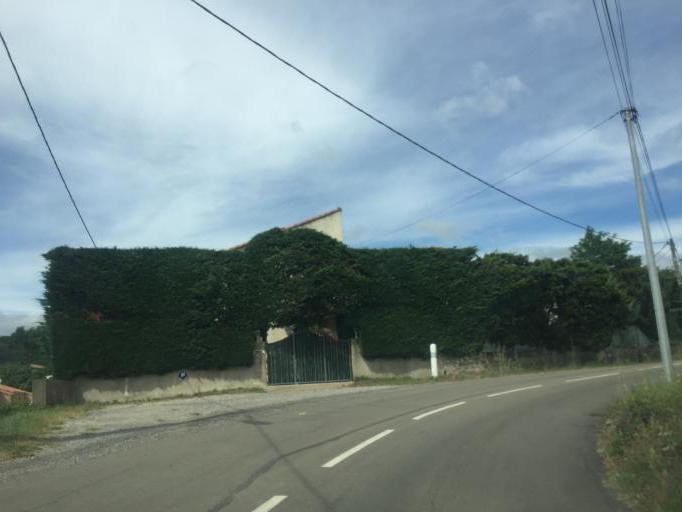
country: FR
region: Rhone-Alpes
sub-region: Departement de l'Ardeche
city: Villeneuve-de-Berg
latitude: 44.5957
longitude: 4.5361
